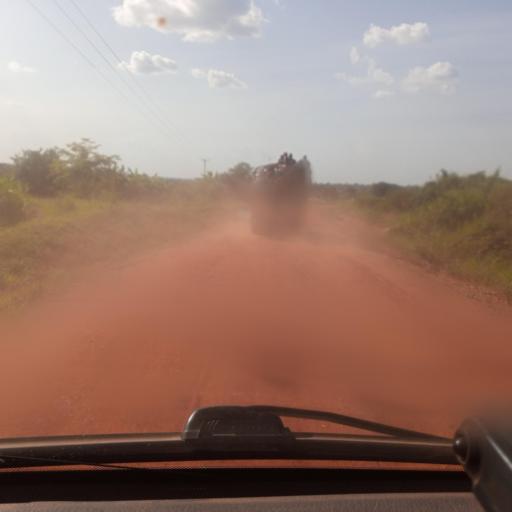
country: UG
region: Northern Region
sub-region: Kitgum District
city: Kitgum
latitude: 3.0016
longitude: 32.9299
